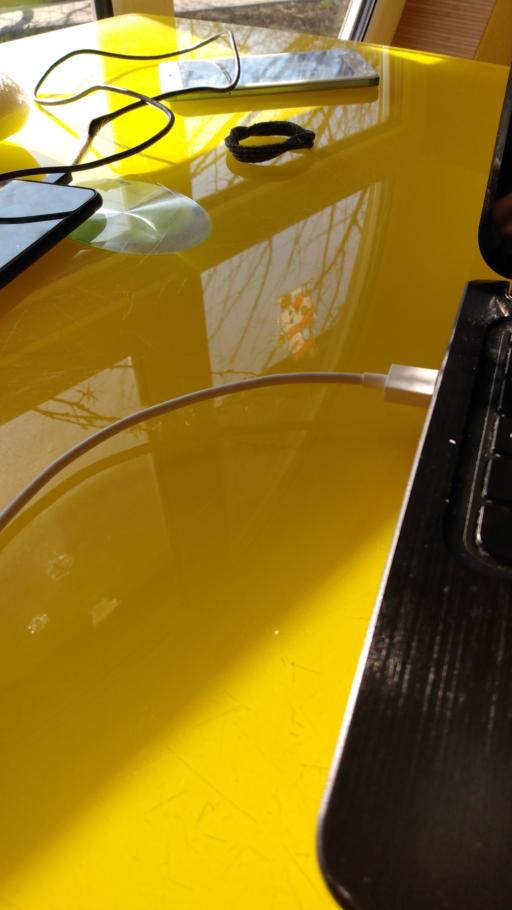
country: RU
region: Novgorod
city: Malaya Vishera
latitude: 58.5063
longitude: 32.2324
